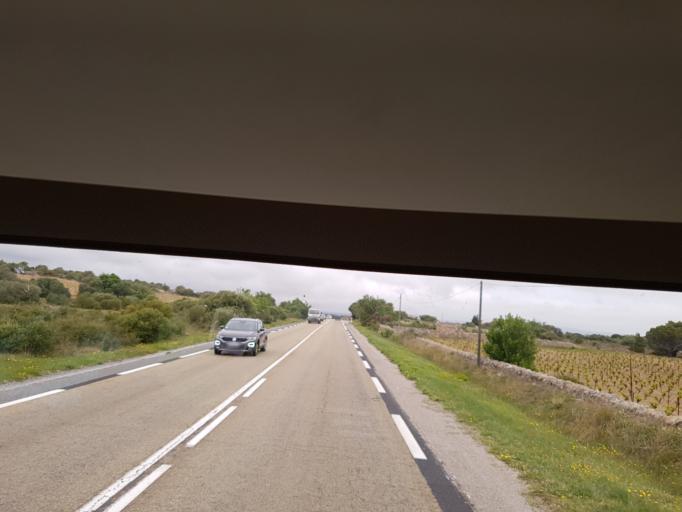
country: FR
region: Languedoc-Roussillon
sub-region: Departement de l'Aude
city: Leucate
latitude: 42.9119
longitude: 2.9986
